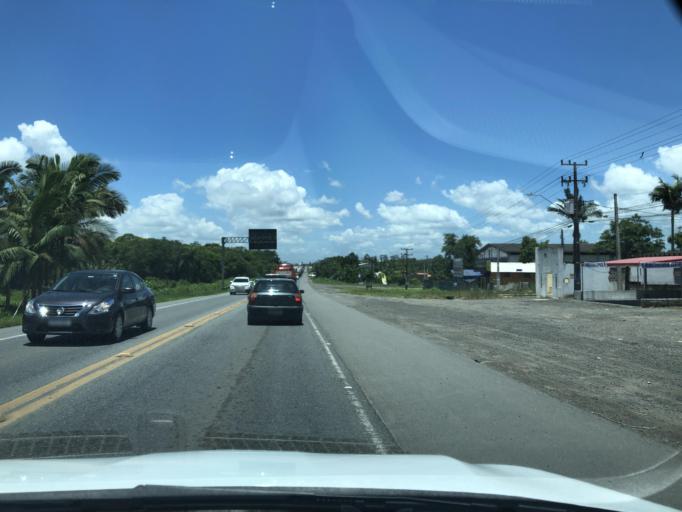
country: BR
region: Santa Catarina
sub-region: Joinville
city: Joinville
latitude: -26.3808
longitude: -48.7236
